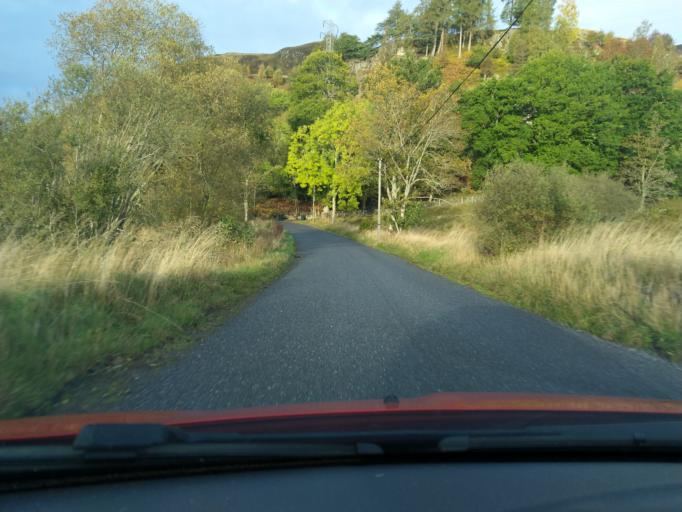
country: GB
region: Scotland
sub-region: Perth and Kinross
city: Aberfeldy
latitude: 56.7040
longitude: -4.1309
